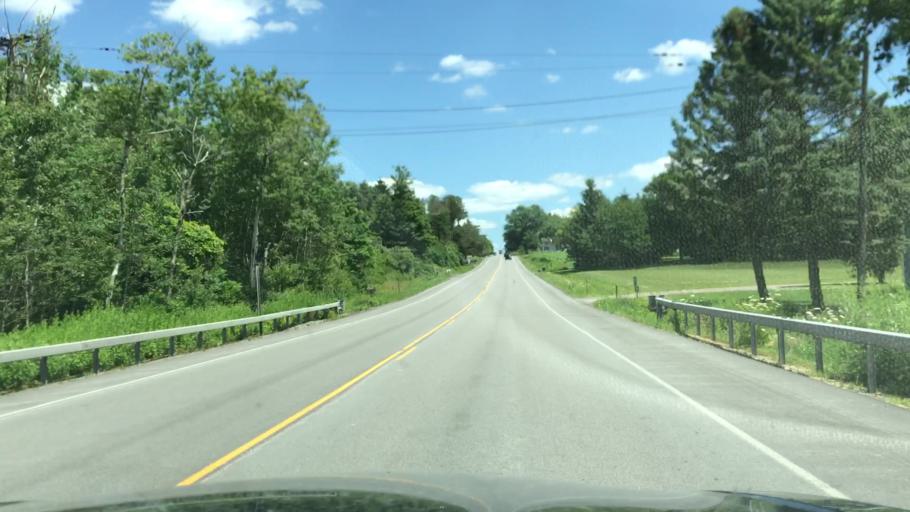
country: US
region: New York
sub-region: Erie County
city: Alden
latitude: 42.7697
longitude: -78.4397
